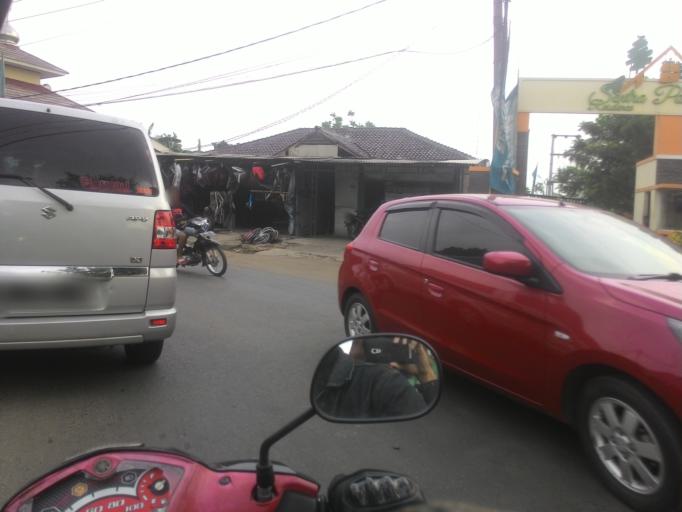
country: ID
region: West Java
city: Cibinong
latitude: -6.4681
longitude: 106.8234
